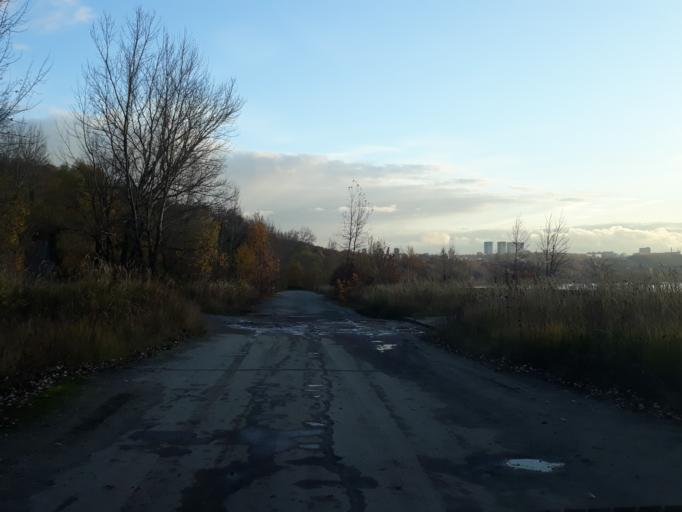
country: RU
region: Nizjnij Novgorod
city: Nizhniy Novgorod
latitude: 56.2732
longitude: 43.9699
